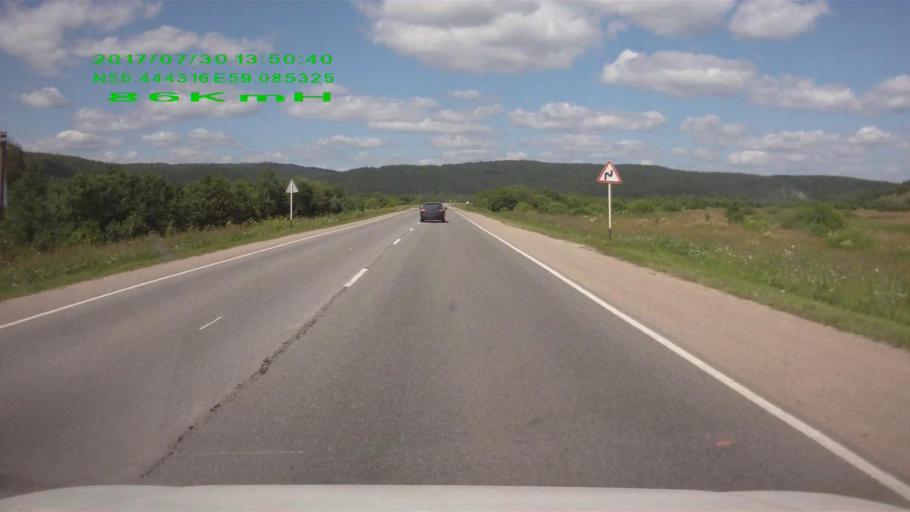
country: RU
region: Sverdlovsk
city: Mikhaylovsk
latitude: 56.4449
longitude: 59.0850
